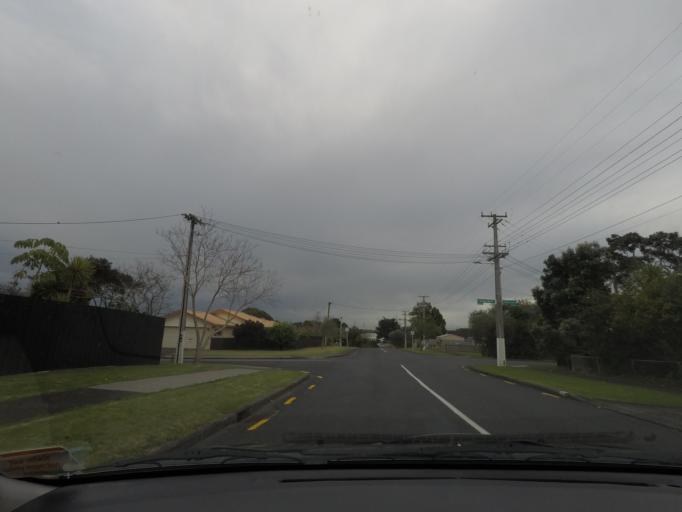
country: NZ
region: Auckland
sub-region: Auckland
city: Rosebank
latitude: -36.8565
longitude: 174.6423
